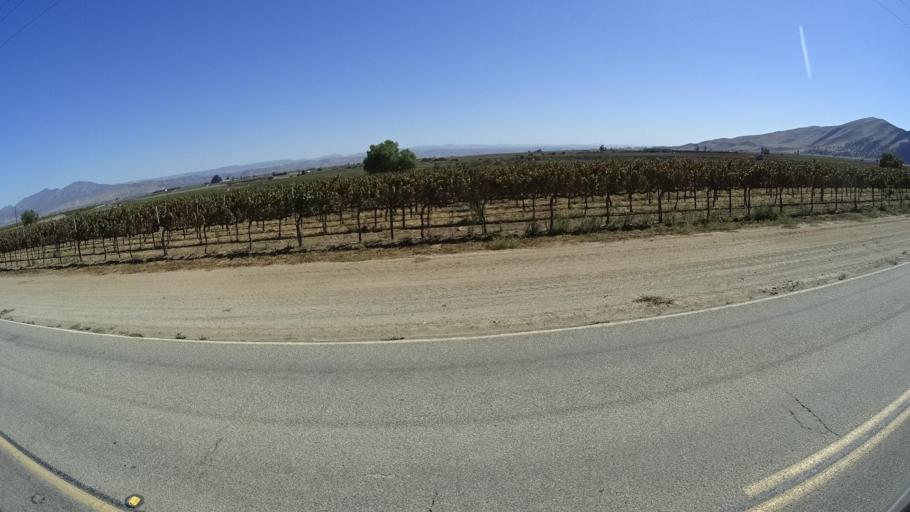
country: US
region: California
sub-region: Monterey County
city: Greenfield
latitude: 36.3059
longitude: -121.3117
